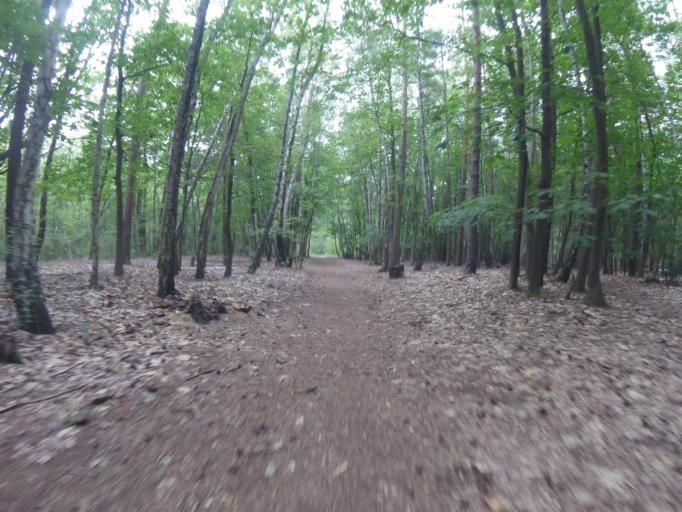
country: DE
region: Brandenburg
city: Bestensee
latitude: 52.2392
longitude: 13.6547
